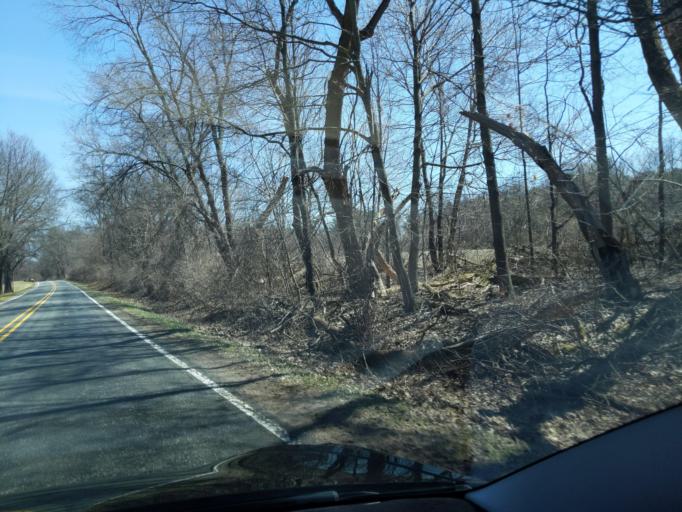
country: US
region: Michigan
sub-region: Ingham County
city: Mason
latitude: 42.5339
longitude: -84.3358
